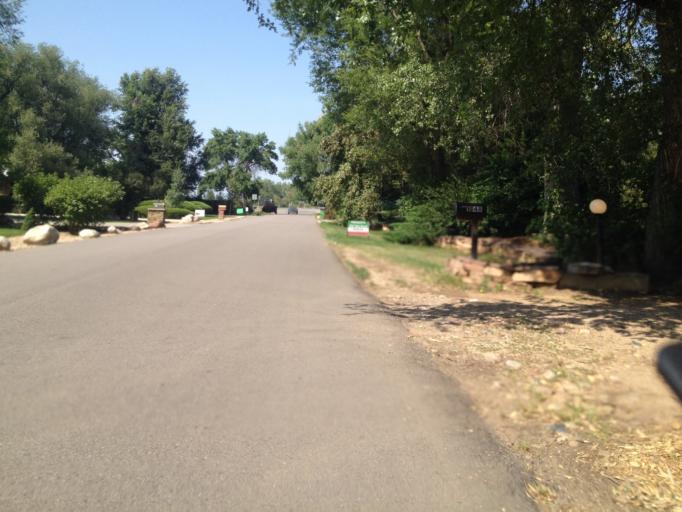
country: US
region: Colorado
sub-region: Boulder County
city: Boulder
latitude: 40.0133
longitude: -105.2156
